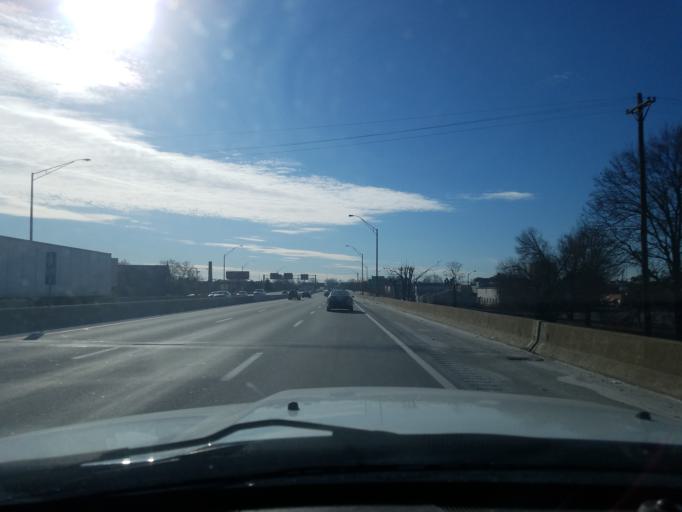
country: US
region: Kentucky
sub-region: Jefferson County
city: Louisville
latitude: 38.2446
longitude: -85.7526
